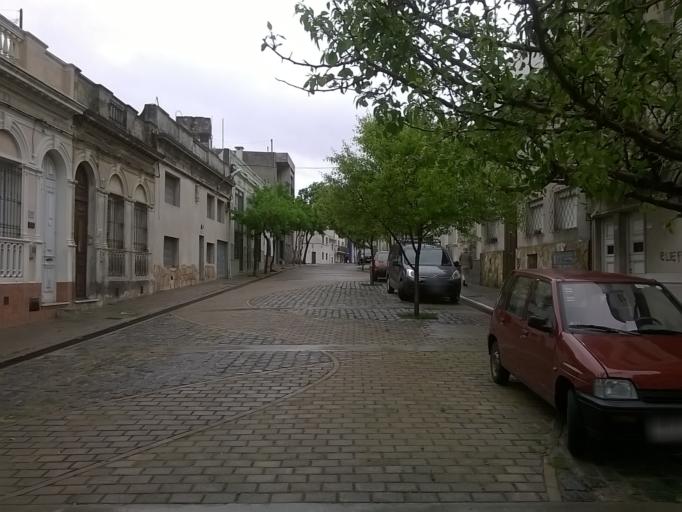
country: UY
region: Montevideo
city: Montevideo
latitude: -34.9094
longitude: -56.1796
